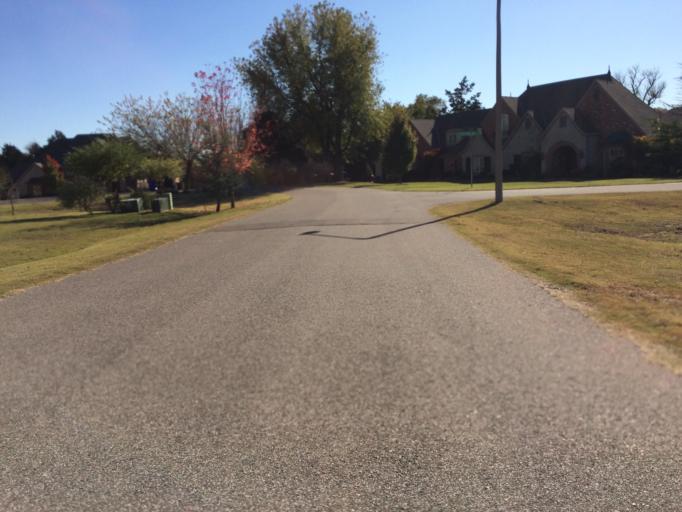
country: US
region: Oklahoma
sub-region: Cleveland County
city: Noble
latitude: 35.1623
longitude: -97.4222
